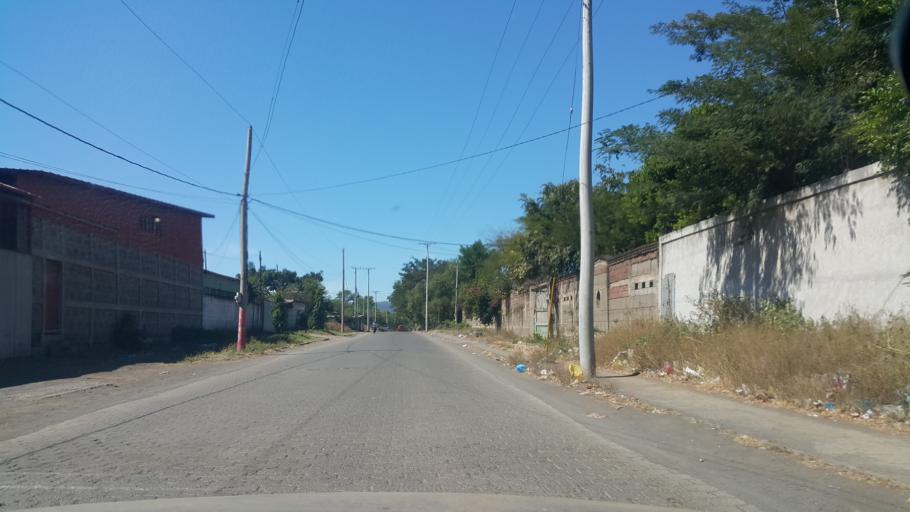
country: NI
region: Managua
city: Ciudad Sandino
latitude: 12.1467
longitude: -86.3386
